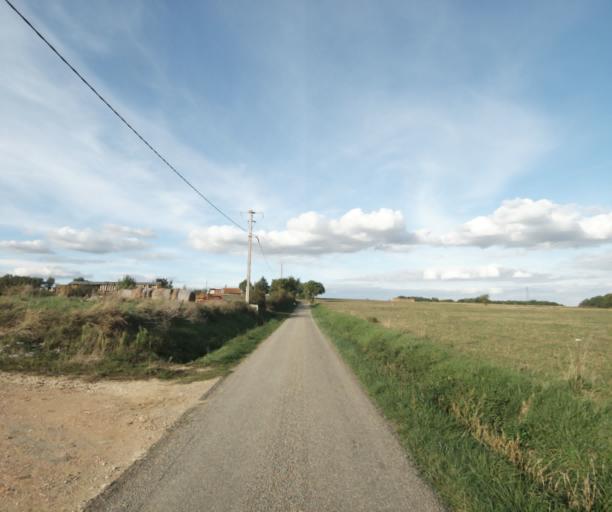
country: FR
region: Midi-Pyrenees
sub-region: Departement du Gers
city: Gondrin
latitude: 43.9093
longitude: 0.2451
